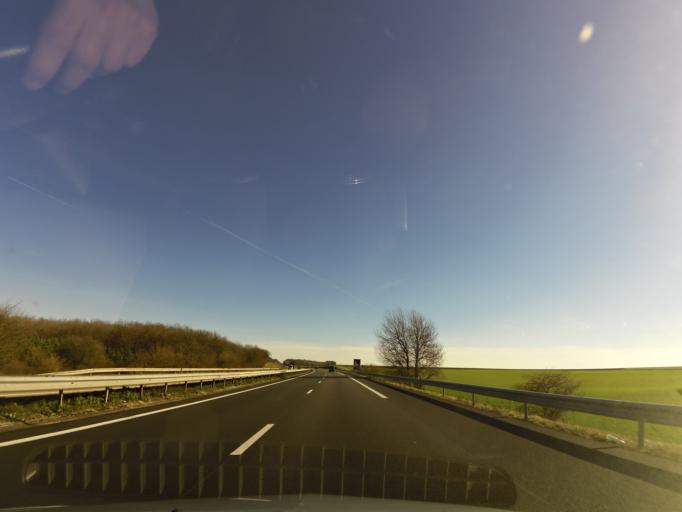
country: FR
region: Bourgogne
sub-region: Departement de l'Yonne
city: Vermenton
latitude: 47.7014
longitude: 3.8068
